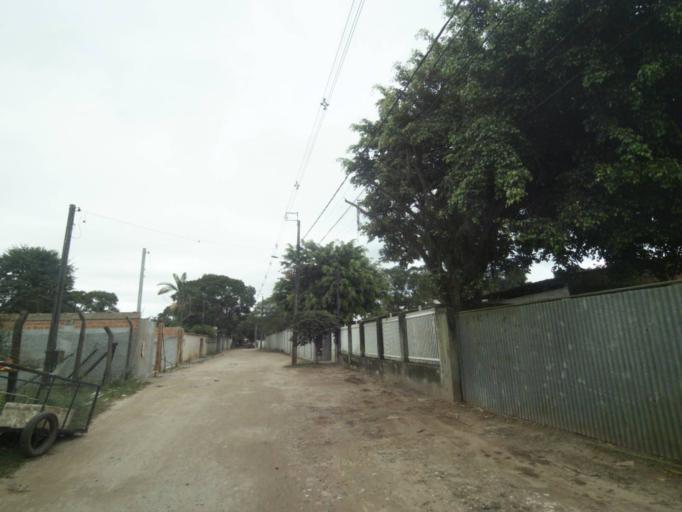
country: BR
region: Parana
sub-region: Paranagua
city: Paranagua
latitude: -25.5367
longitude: -48.5489
